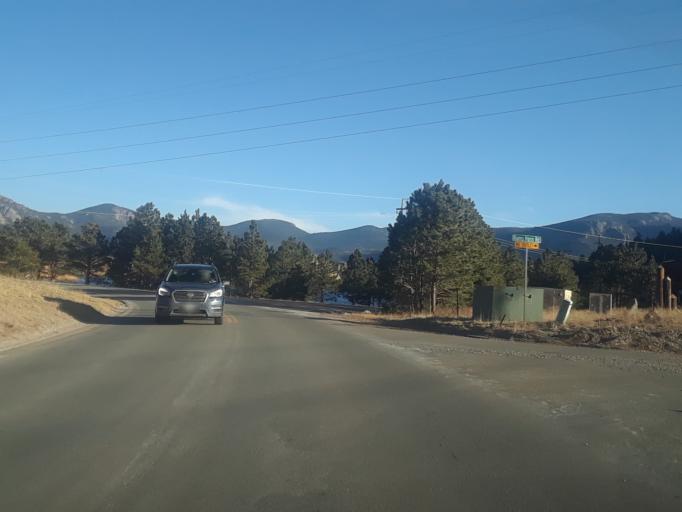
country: US
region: Colorado
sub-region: Larimer County
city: Estes Park
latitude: 40.3475
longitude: -105.5381
